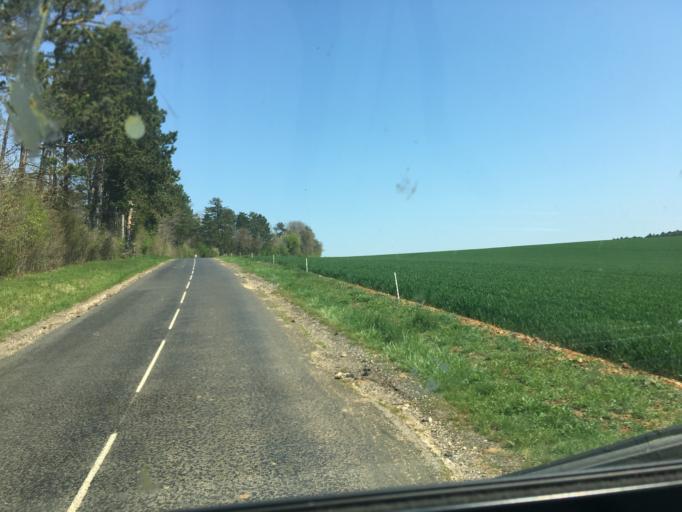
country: FR
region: Lorraine
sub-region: Departement de Meurthe-et-Moselle
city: Montauville
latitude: 48.9048
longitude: 5.9183
